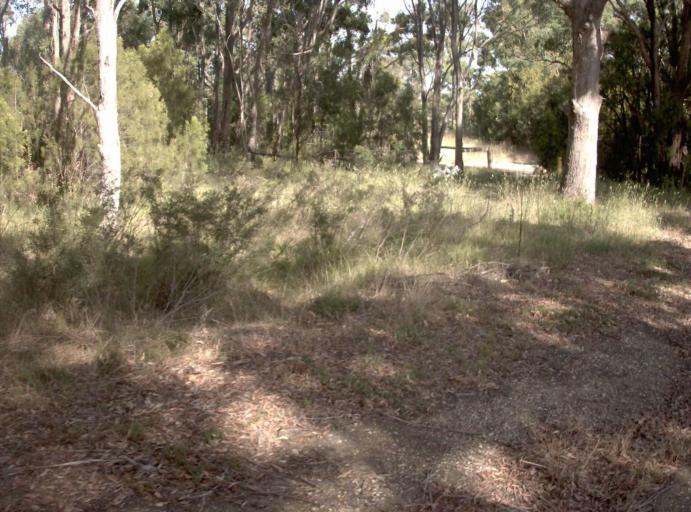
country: AU
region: Victoria
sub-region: East Gippsland
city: Lakes Entrance
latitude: -37.7928
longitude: 147.8309
